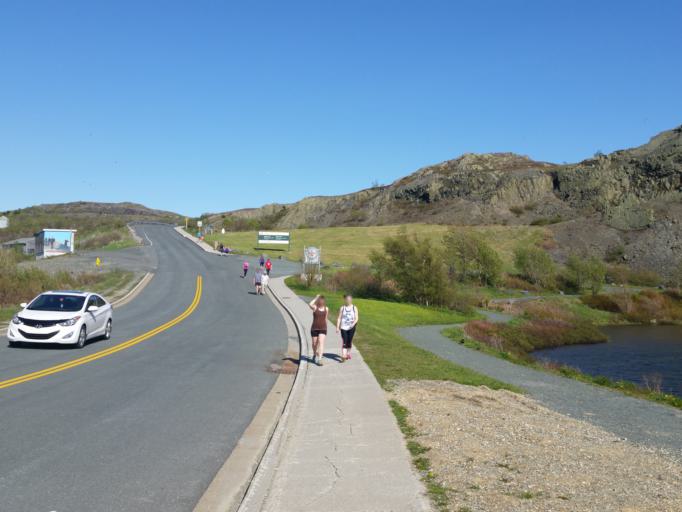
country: CA
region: Newfoundland and Labrador
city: St. John's
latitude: 47.5721
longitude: -52.6904
